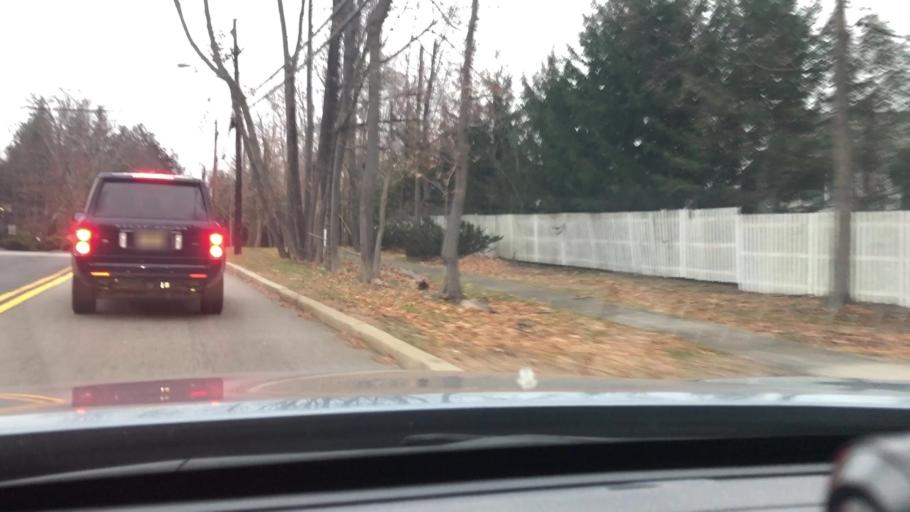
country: US
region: New Jersey
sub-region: Bergen County
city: Woodcliff Lake
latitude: 41.0052
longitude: -74.0738
